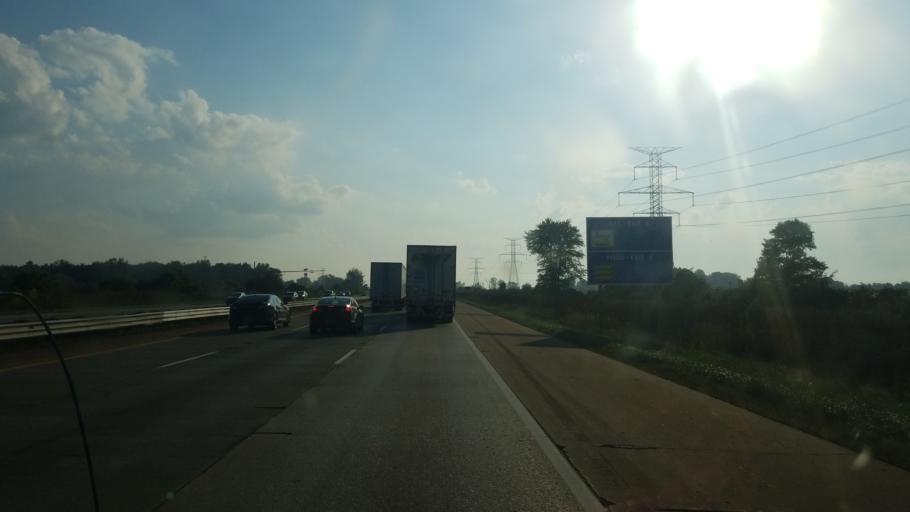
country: US
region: Michigan
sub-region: Monroe County
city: Luna Pier
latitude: 41.8183
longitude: -83.4418
